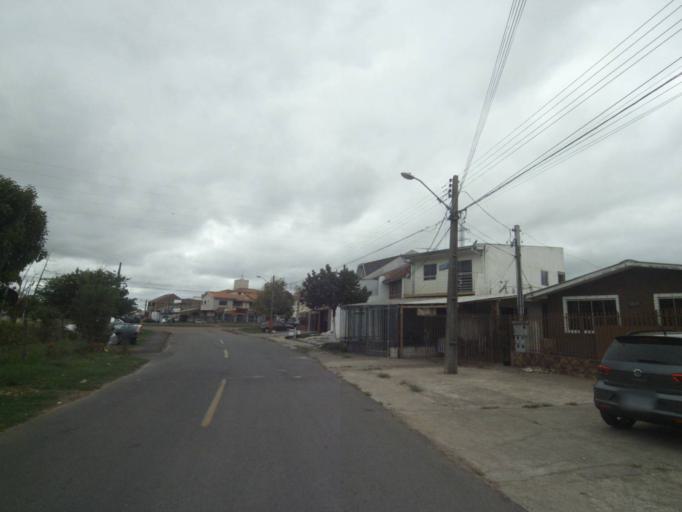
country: BR
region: Parana
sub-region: Sao Jose Dos Pinhais
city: Sao Jose dos Pinhais
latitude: -25.5430
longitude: -49.2706
